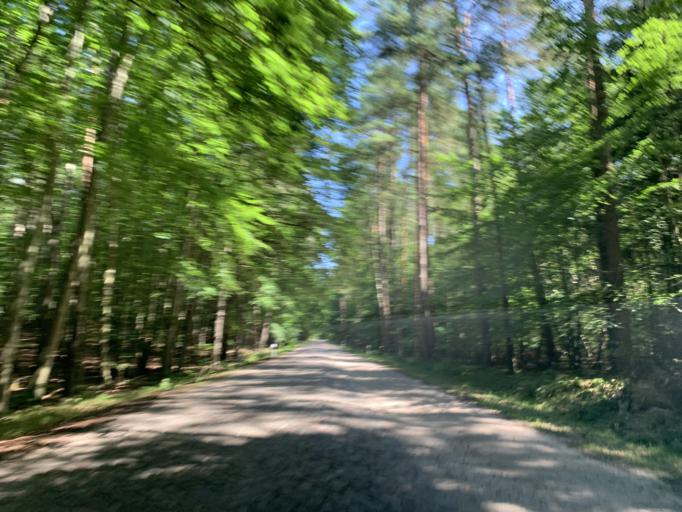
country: DE
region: Mecklenburg-Vorpommern
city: Carpin
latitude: 53.3175
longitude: 13.2716
